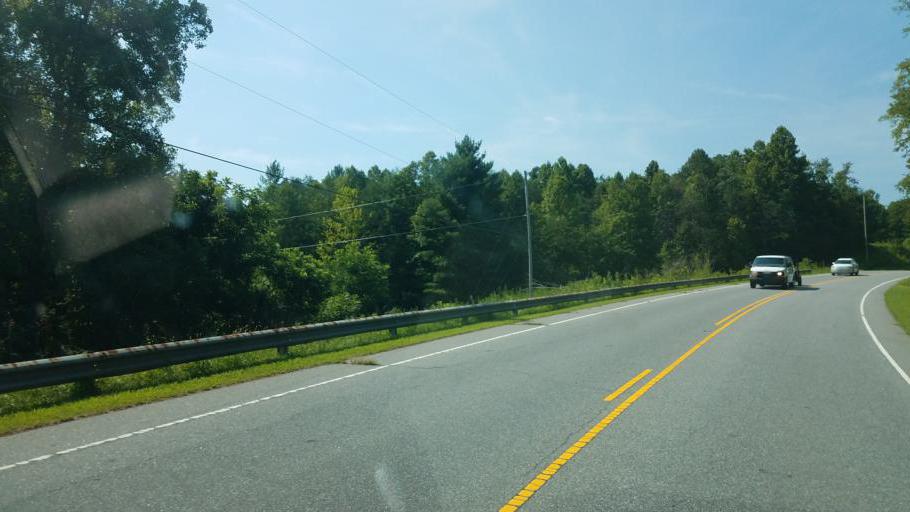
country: US
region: North Carolina
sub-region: Burke County
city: Glen Alpine
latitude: 35.8364
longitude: -81.7773
